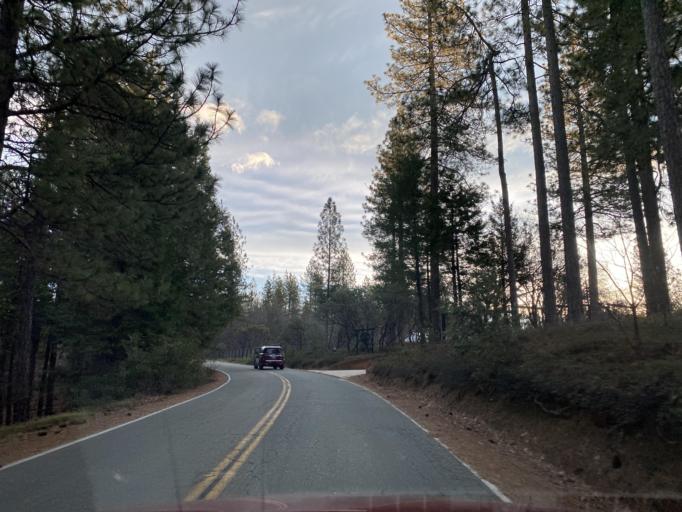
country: US
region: California
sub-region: Amador County
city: Pioneer
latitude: 38.4996
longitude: -120.6164
